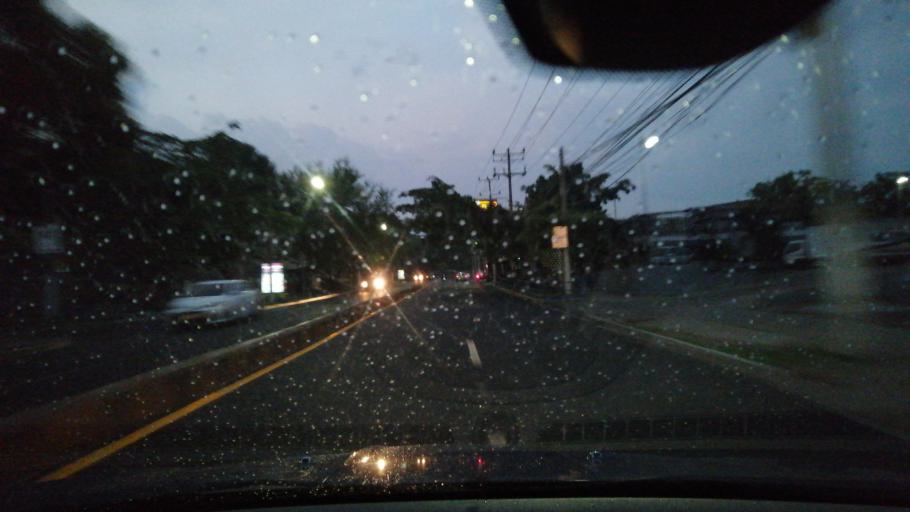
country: SV
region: San Salvador
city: San Salvador
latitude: 13.7083
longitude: -89.2040
